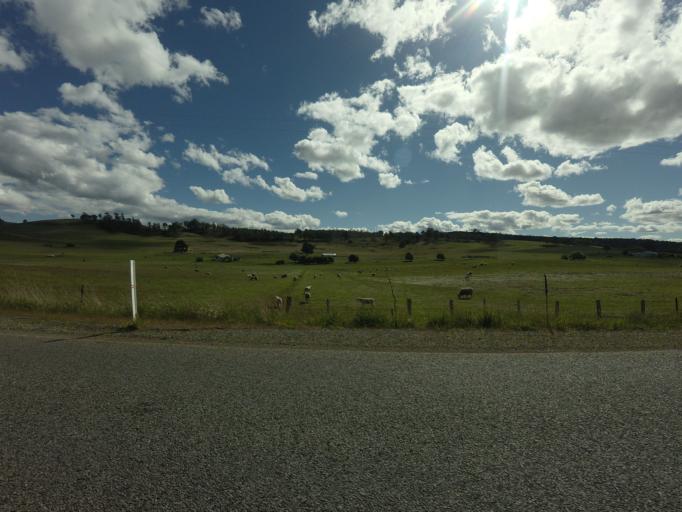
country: AU
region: Tasmania
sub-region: Brighton
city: Bridgewater
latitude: -42.4819
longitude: 147.3274
